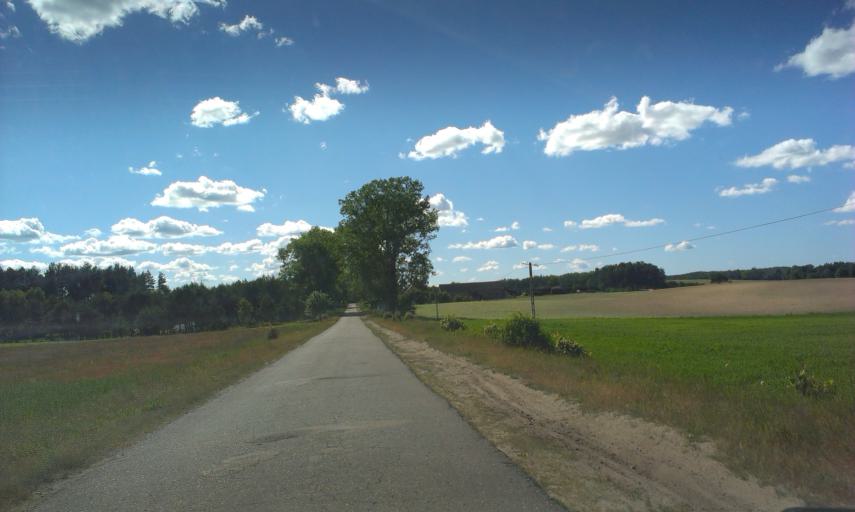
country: PL
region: West Pomeranian Voivodeship
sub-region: Powiat szczecinecki
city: Szczecinek
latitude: 53.8016
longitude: 16.6721
